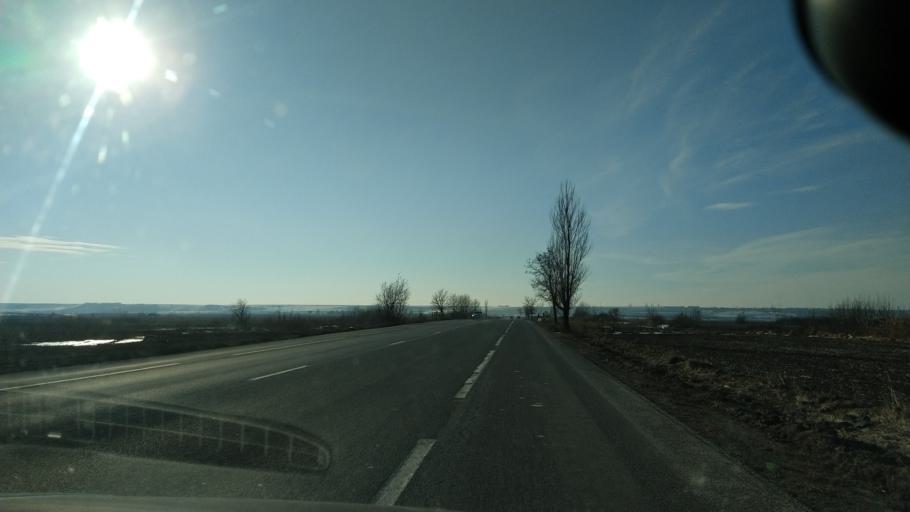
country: RO
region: Iasi
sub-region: Comuna Butea
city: Butea
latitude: 47.0729
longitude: 26.8897
